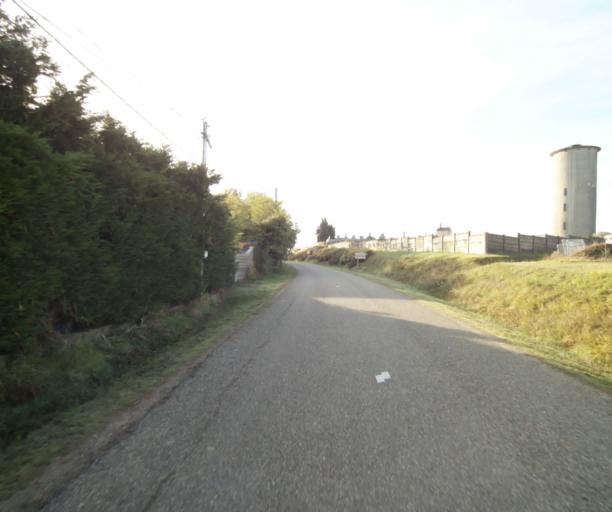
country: FR
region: Midi-Pyrenees
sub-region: Departement de la Haute-Garonne
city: Villemur-sur-Tarn
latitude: 43.9042
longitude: 1.4925
